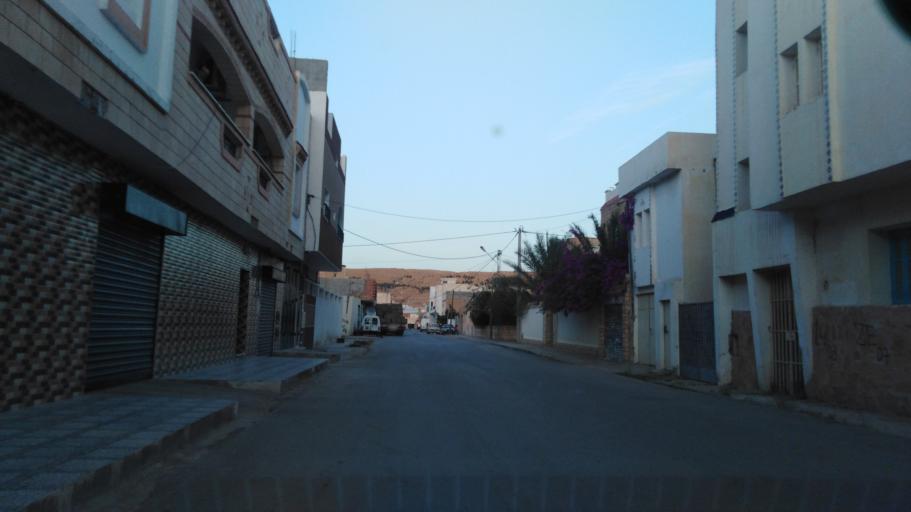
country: TN
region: Tataouine
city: Tataouine
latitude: 32.9377
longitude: 10.4518
